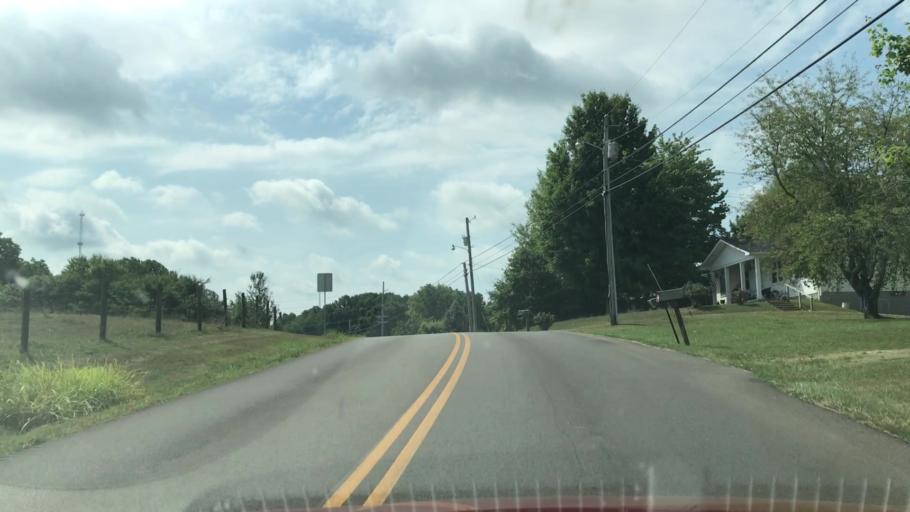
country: US
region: Kentucky
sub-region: Barren County
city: Glasgow
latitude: 36.9824
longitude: -85.9031
